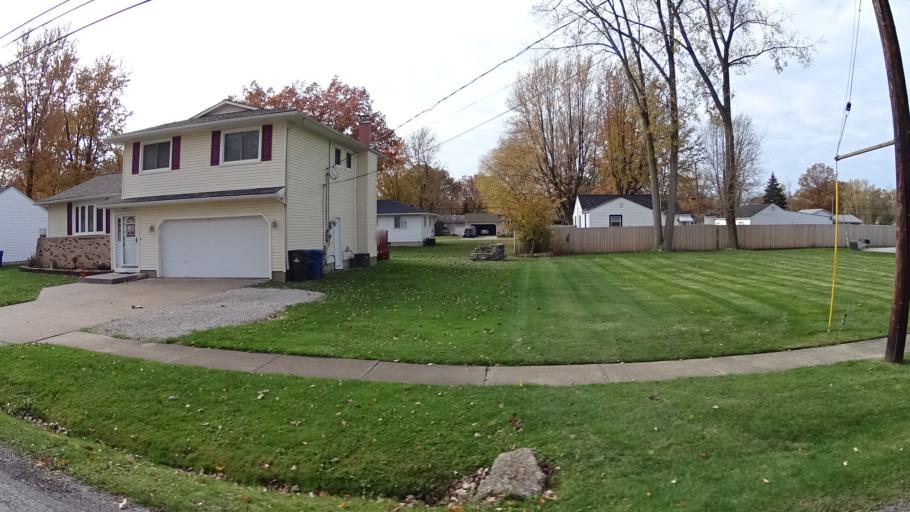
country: US
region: Ohio
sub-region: Lorain County
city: Sheffield Lake
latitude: 41.4866
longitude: -82.0966
